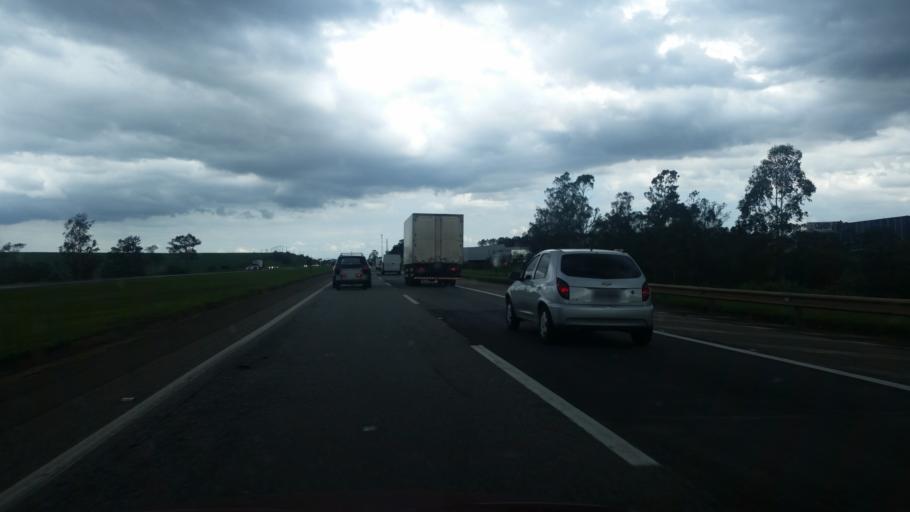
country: BR
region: Sao Paulo
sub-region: Porto Feliz
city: Porto Feliz
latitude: -23.3453
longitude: -47.5275
